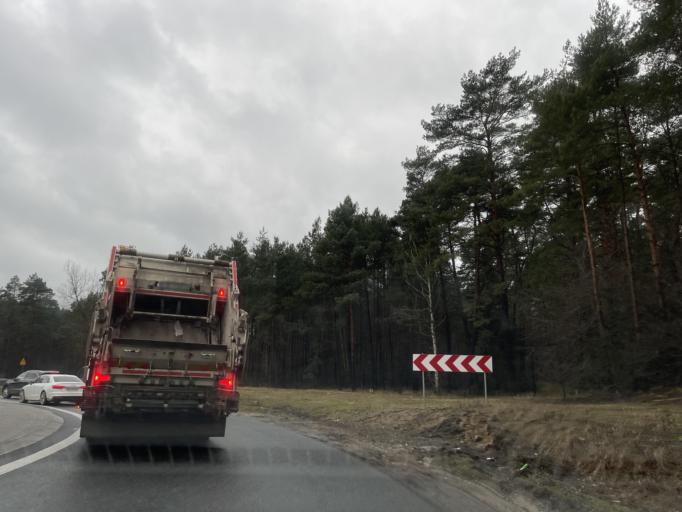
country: PL
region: Kujawsko-Pomorskie
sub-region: Powiat bydgoski
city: Nowa Wies Wielka
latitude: 53.0607
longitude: 18.0823
